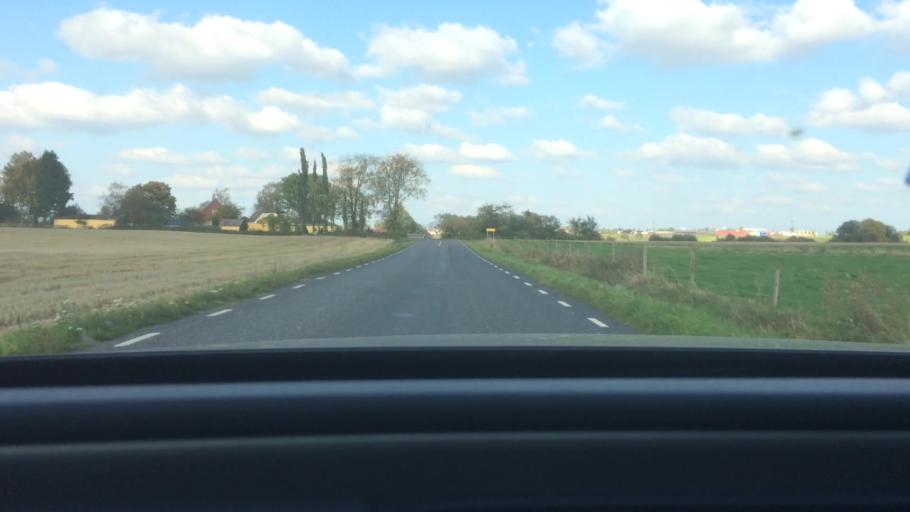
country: SE
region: Vaestra Goetaland
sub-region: Falkopings Kommun
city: Falkoeping
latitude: 58.1432
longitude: 13.5435
